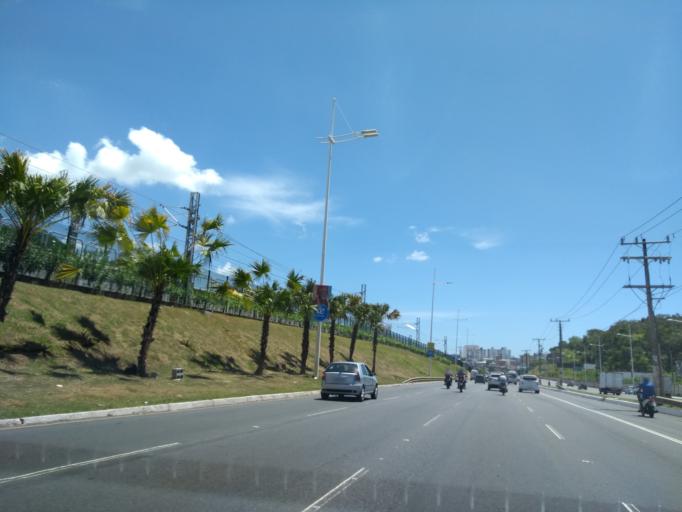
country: BR
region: Bahia
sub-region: Salvador
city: Salvador
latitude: -12.9730
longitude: -38.4480
